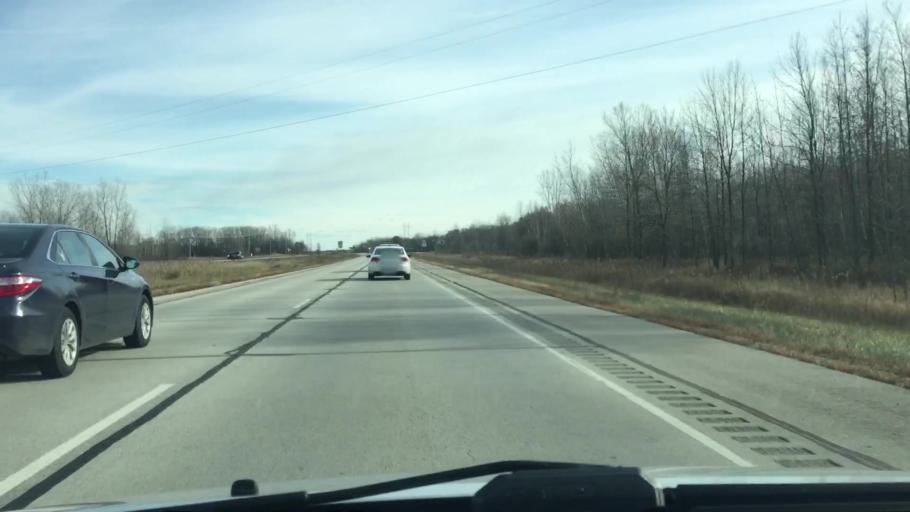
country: US
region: Wisconsin
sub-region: Brown County
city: Oneida
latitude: 44.5868
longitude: -88.1955
